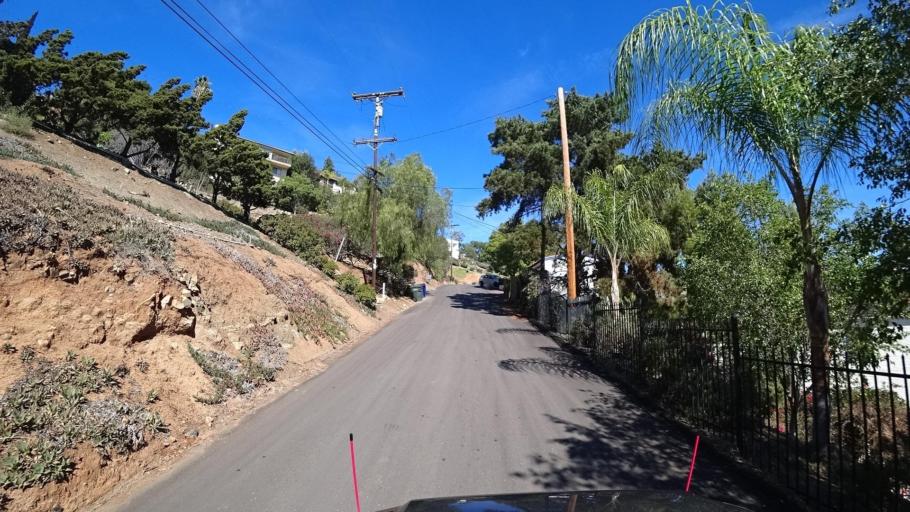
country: US
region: California
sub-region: San Diego County
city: Casa de Oro-Mount Helix
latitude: 32.7588
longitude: -116.9672
